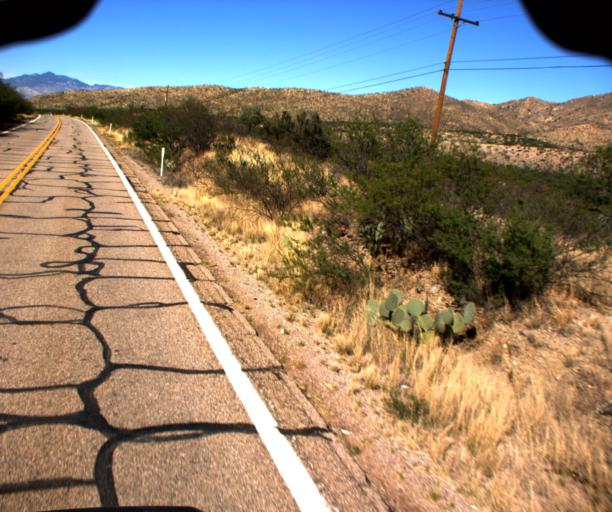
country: US
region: Arizona
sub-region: Pima County
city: Corona de Tucson
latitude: 31.8897
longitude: -110.6686
